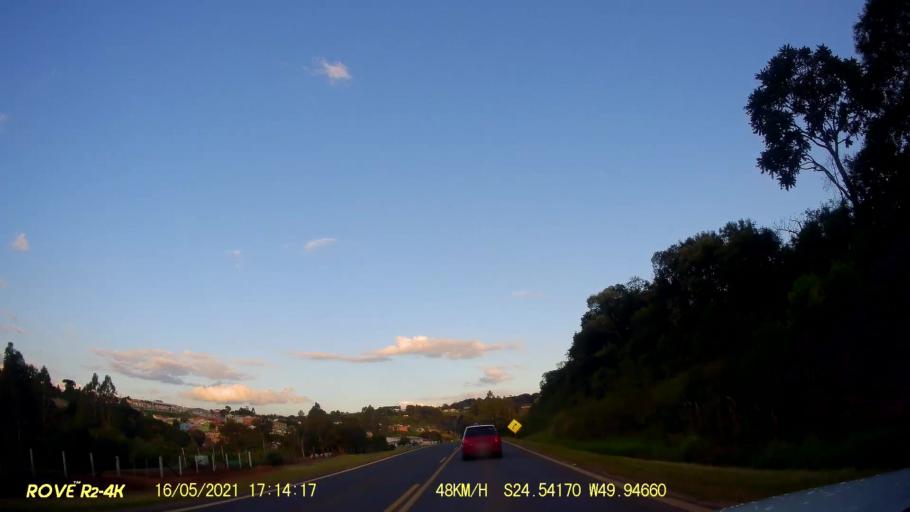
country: BR
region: Parana
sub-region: Pirai Do Sul
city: Pirai do Sul
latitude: -24.5418
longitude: -49.9464
